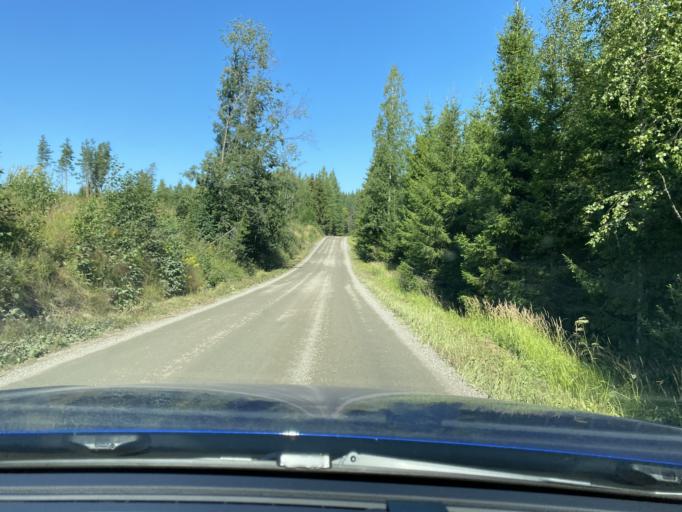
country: FI
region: Central Finland
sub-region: Jyvaeskylae
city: Korpilahti
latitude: 61.8686
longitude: 25.4221
